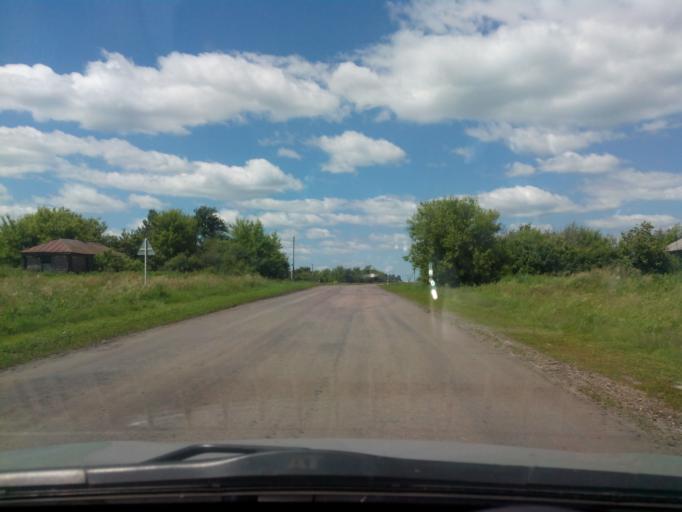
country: RU
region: Voronezj
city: Gribanovskiy
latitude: 51.6272
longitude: 41.8957
